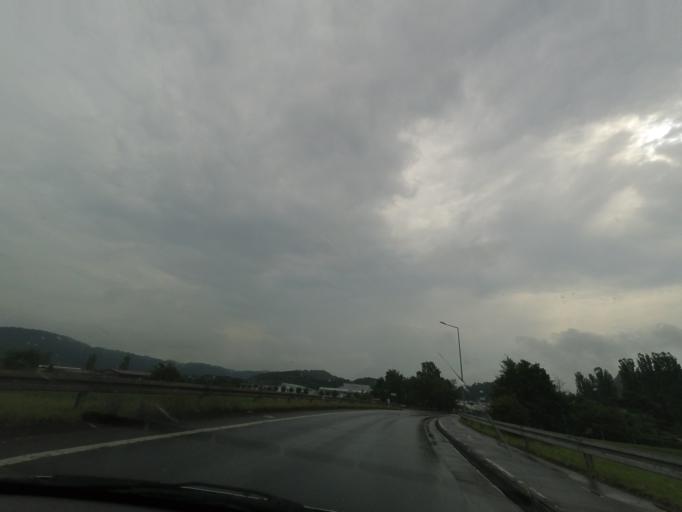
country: DE
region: Hesse
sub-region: Regierungsbezirk Giessen
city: Marburg an der Lahn
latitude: 50.8395
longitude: 8.7627
